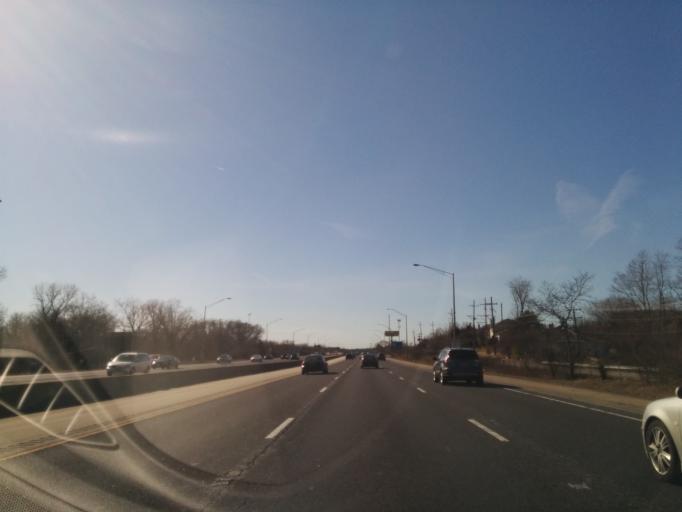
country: US
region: Illinois
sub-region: DuPage County
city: Darien
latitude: 41.7373
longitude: -87.9563
